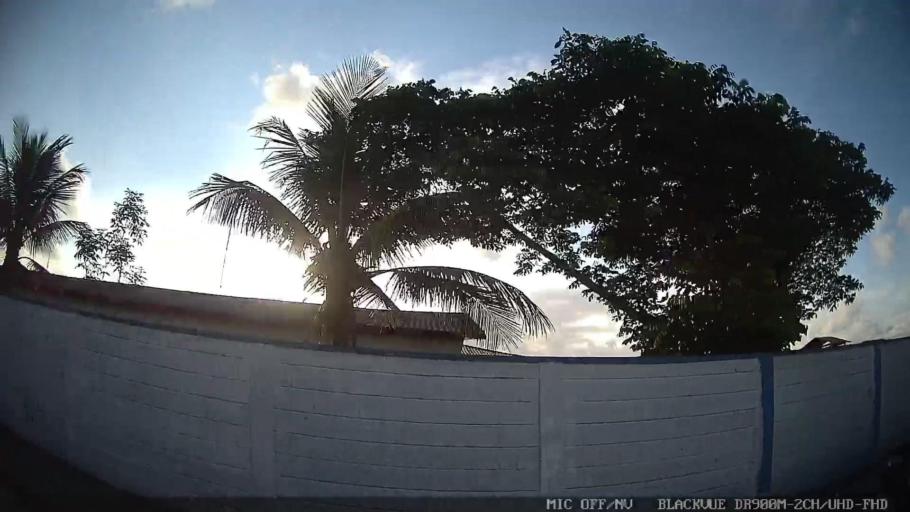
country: BR
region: Sao Paulo
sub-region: Itanhaem
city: Itanhaem
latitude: -24.1829
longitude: -46.8302
